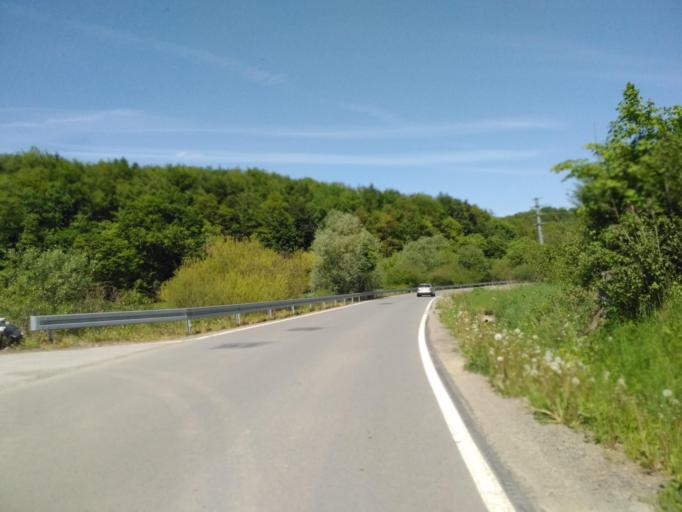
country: PL
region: Subcarpathian Voivodeship
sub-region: Powiat krosnienski
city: Dukla
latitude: 49.5803
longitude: 21.6945
